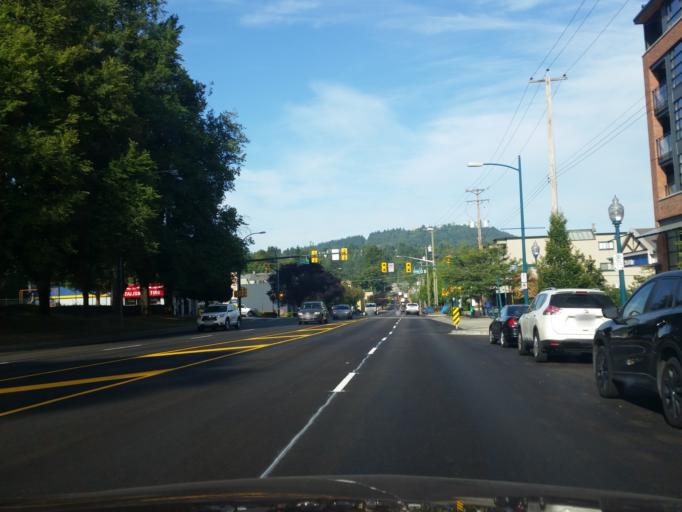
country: CA
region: British Columbia
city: Port Moody
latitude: 49.2768
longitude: -122.8511
